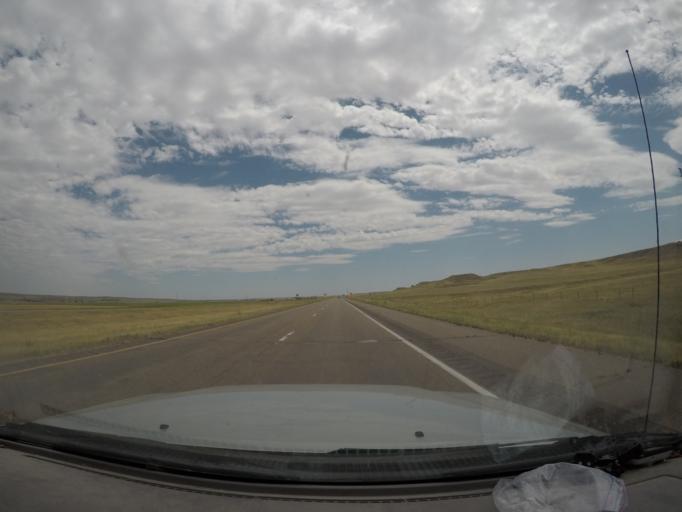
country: US
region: Nebraska
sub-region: Cheyenne County
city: Sidney
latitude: 41.1611
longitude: -103.0969
